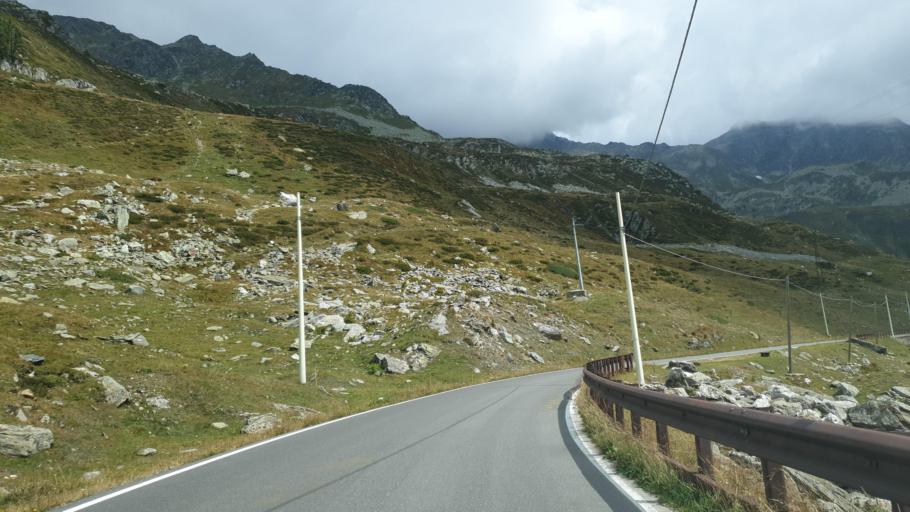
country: IT
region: Lombardy
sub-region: Provincia di Sondrio
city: Campodolcino
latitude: 46.4900
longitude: 9.3386
